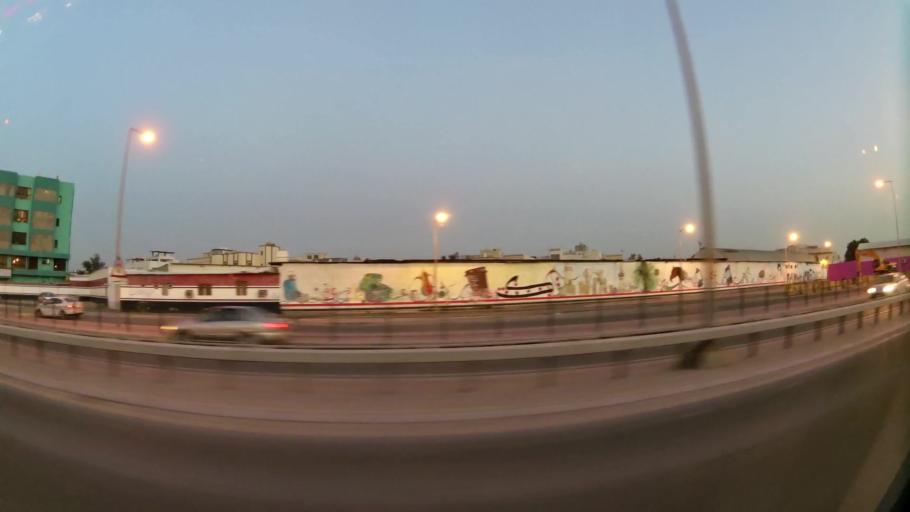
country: BH
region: Manama
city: Jidd Hafs
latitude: 26.2108
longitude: 50.5548
